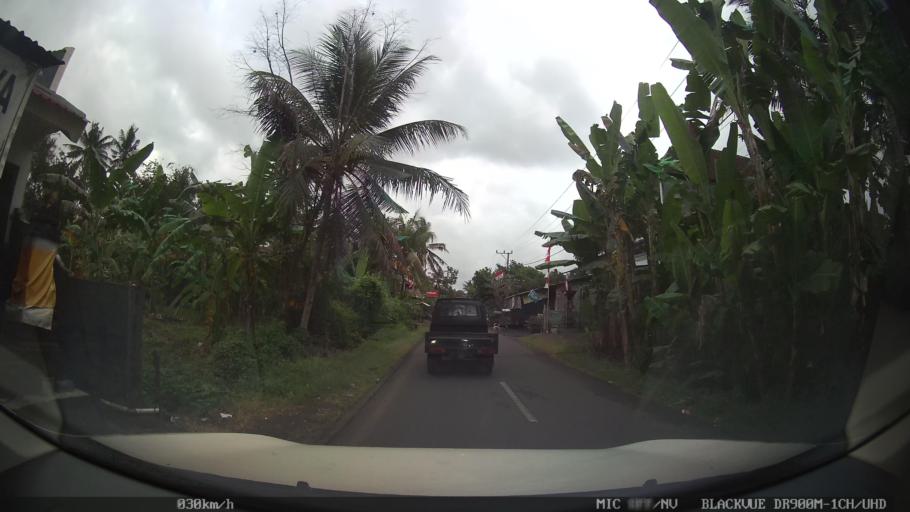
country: ID
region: Bali
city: Banjar Parekan
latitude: -8.5694
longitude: 115.2098
